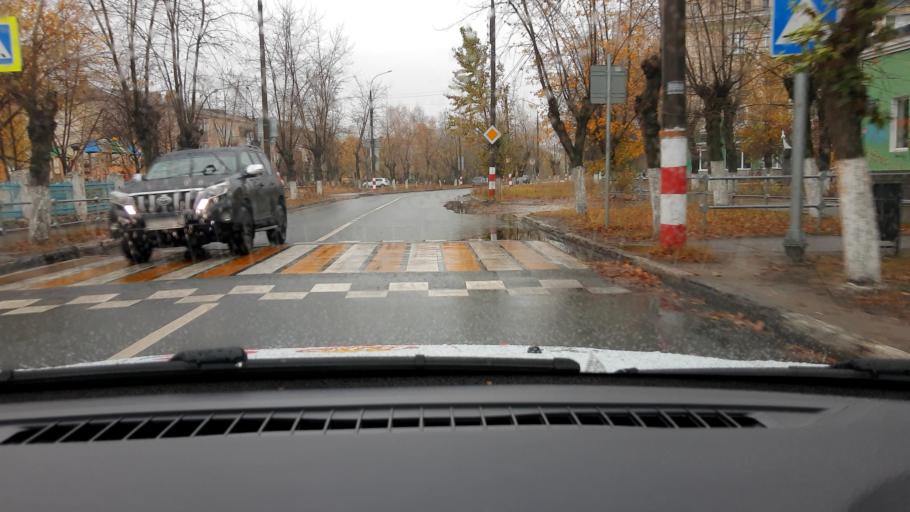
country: RU
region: Nizjnij Novgorod
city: Dzerzhinsk
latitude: 56.2396
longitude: 43.4559
